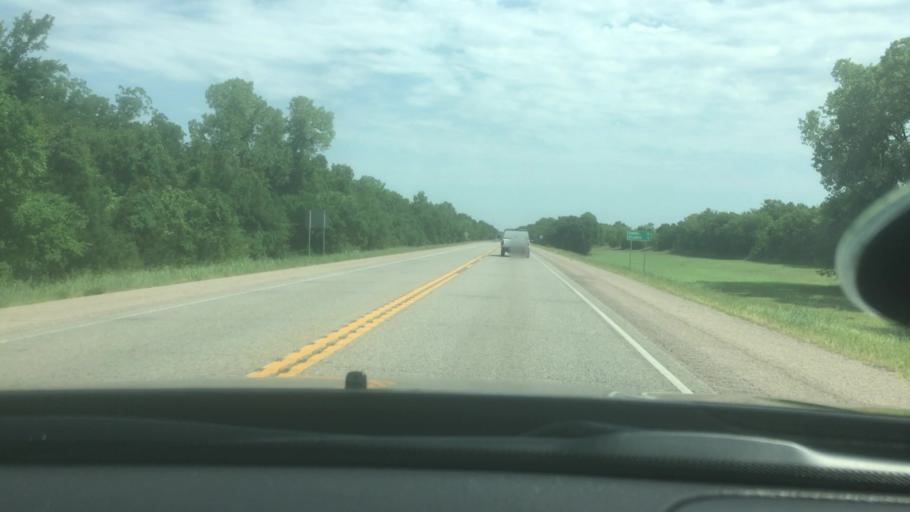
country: US
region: Oklahoma
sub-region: Seminole County
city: Maud
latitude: 35.0744
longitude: -96.9312
